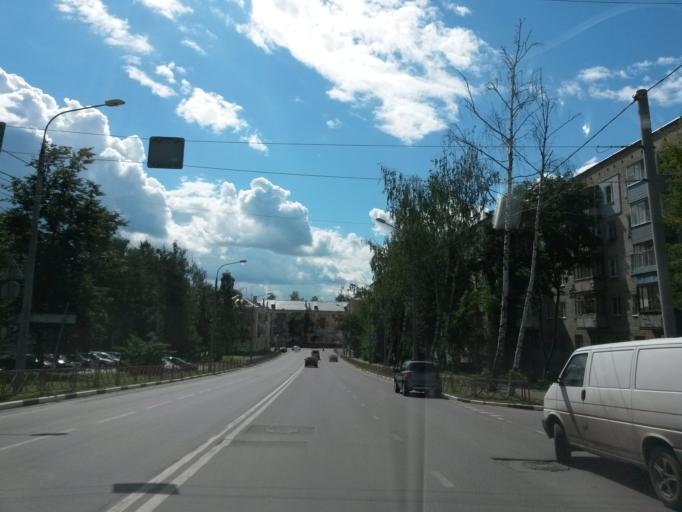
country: RU
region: Jaroslavl
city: Yaroslavl
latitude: 57.6233
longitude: 39.8680
